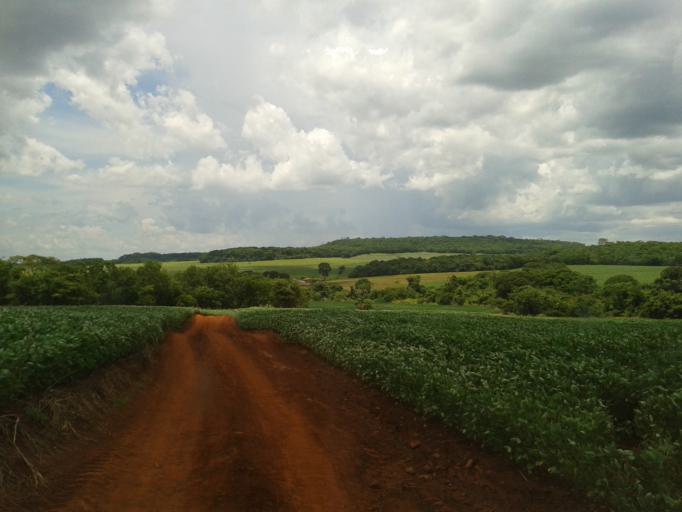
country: BR
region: Minas Gerais
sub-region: Centralina
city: Centralina
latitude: -18.6836
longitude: -49.2189
